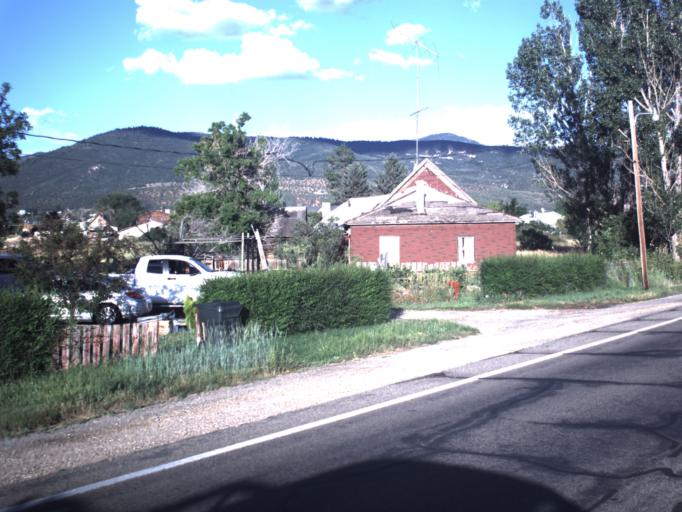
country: US
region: Utah
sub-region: Sanpete County
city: Fairview
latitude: 39.6357
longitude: -111.4432
